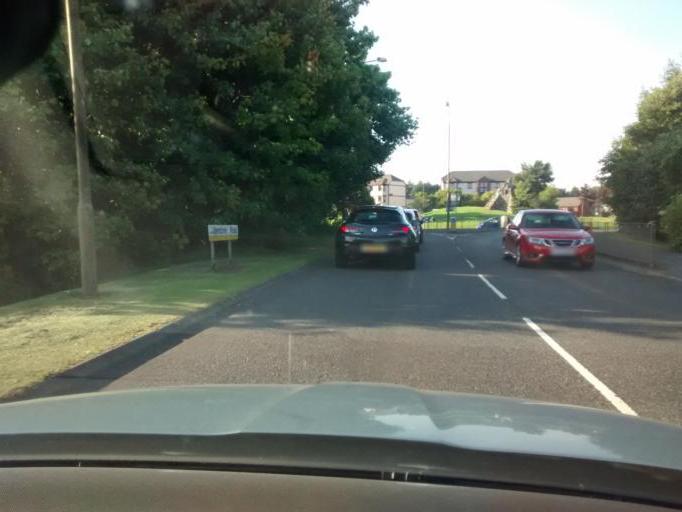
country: GB
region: Scotland
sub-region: West Lothian
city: Livingston
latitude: 55.8998
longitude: -3.5374
